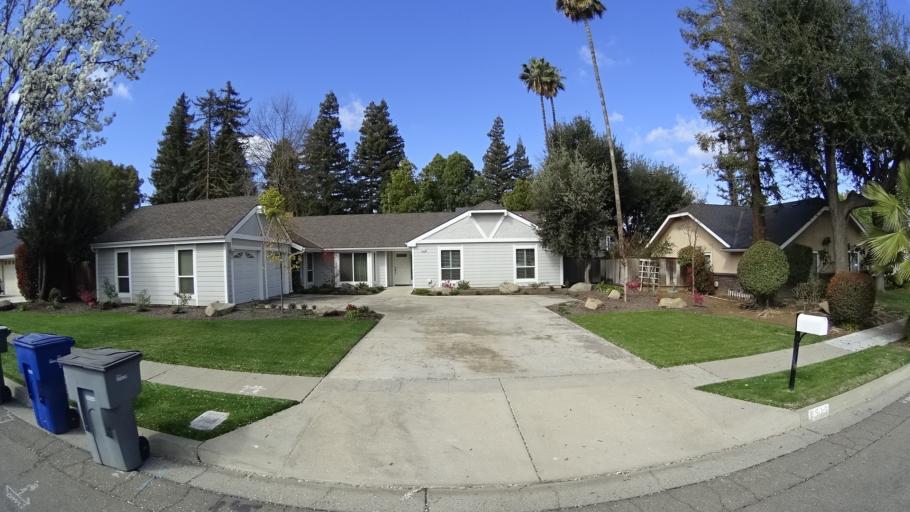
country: US
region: California
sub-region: Fresno County
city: Fresno
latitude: 36.8340
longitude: -119.8535
